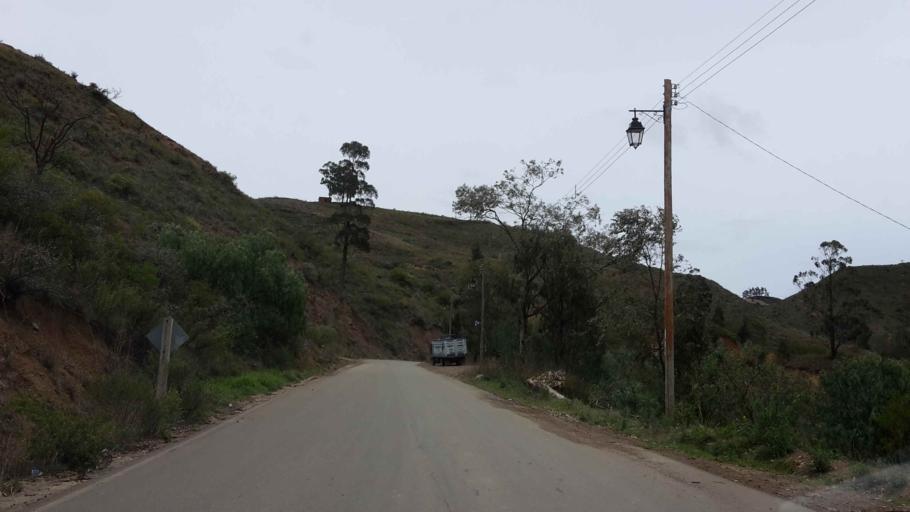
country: BO
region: Cochabamba
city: Totora
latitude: -17.7295
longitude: -65.1912
